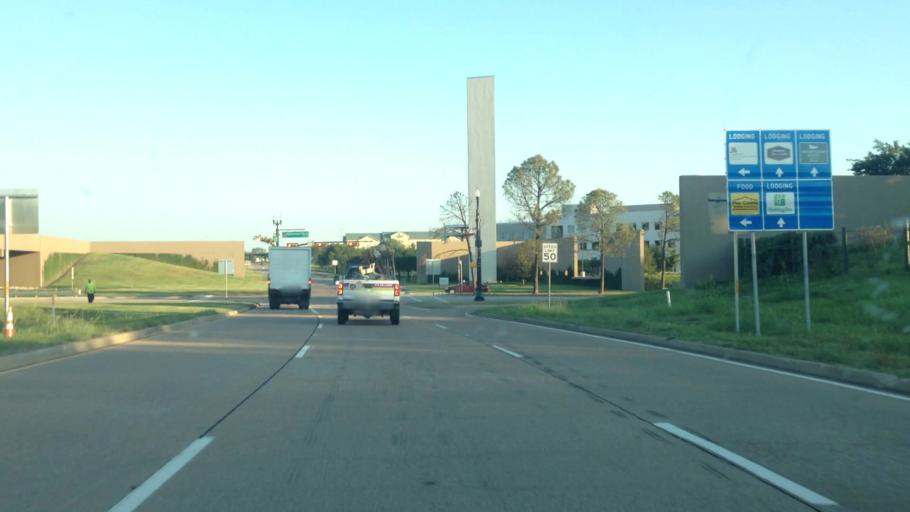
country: US
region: Texas
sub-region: Denton County
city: Trophy Club
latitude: 32.9815
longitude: -97.1661
